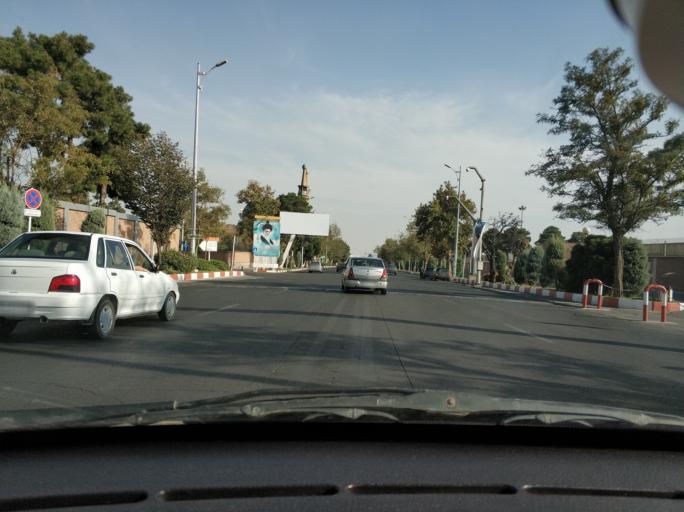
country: IR
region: Tehran
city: Tehran
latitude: 35.6927
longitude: 51.3256
